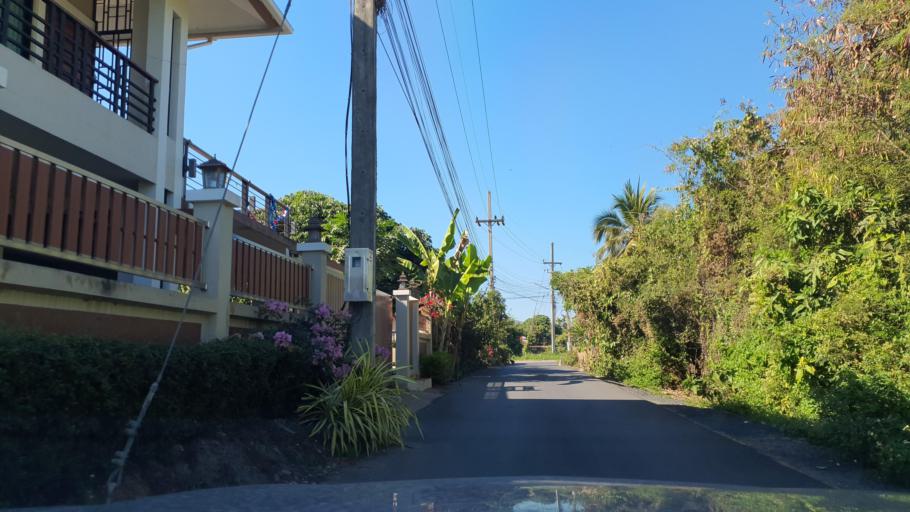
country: TH
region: Chiang Mai
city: San Pa Tong
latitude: 18.6587
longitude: 98.8724
